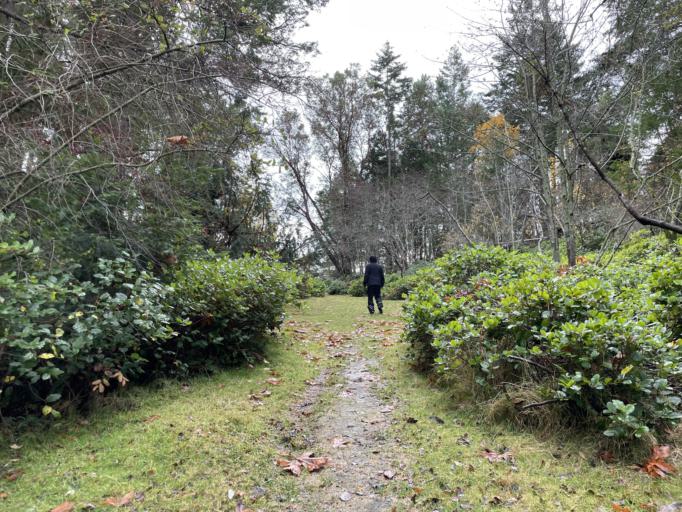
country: CA
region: British Columbia
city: North Cowichan
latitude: 48.9386
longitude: -123.5443
